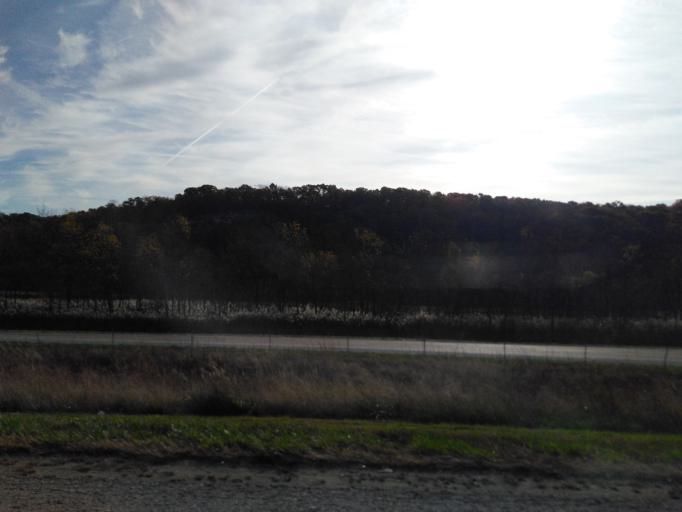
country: US
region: Illinois
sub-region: Saint Clair County
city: Dupo
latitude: 38.5023
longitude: -90.2095
